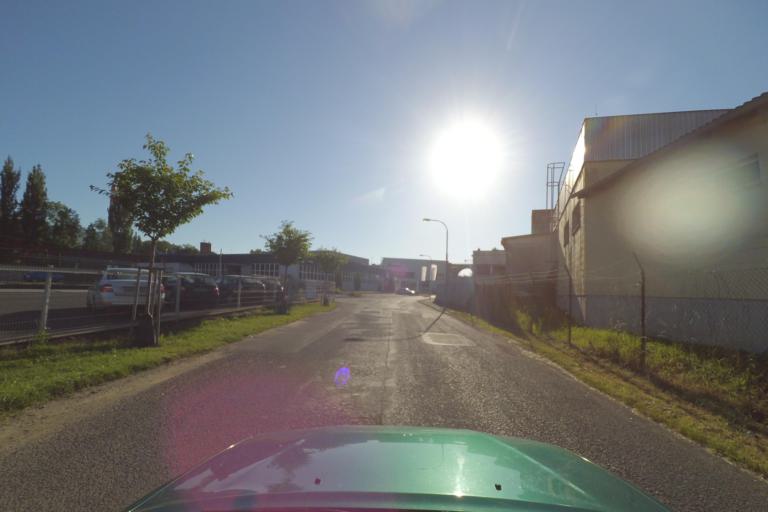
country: CZ
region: Karlovarsky
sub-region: Okres Cheb
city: Cheb
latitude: 50.0845
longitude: 12.3800
